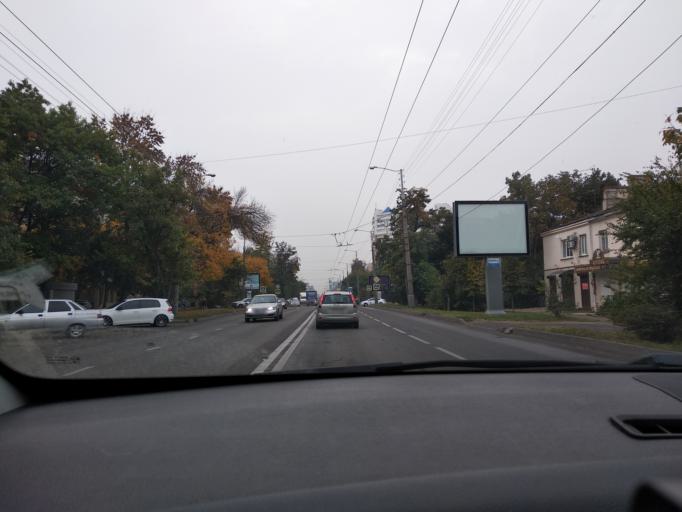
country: RU
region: Krasnodarskiy
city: Krasnodar
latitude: 45.0553
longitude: 38.9604
